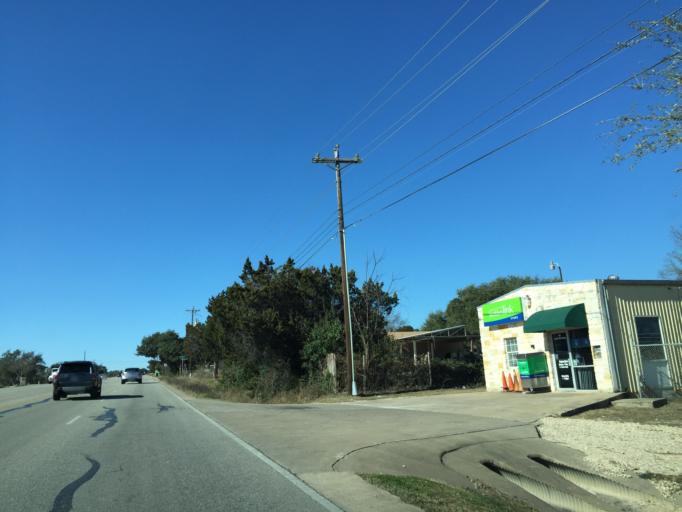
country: US
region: Texas
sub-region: Williamson County
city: Leander
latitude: 30.5566
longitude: -97.8486
